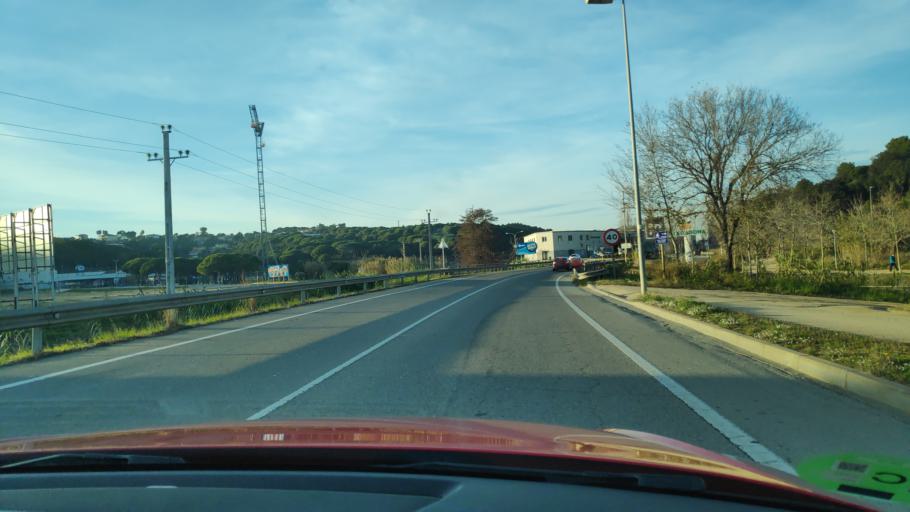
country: ES
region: Catalonia
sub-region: Provincia de Girona
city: Lloret de Mar
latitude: 41.7079
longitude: 2.8334
